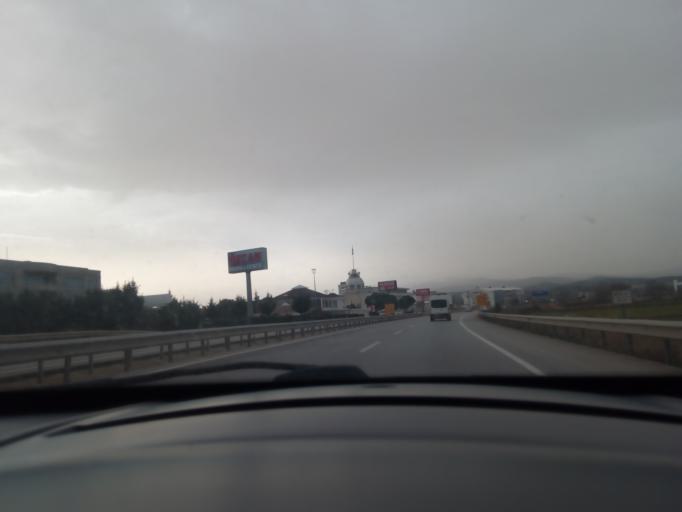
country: TR
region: Bursa
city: Tatkavakli
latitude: 40.0402
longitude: 28.3777
